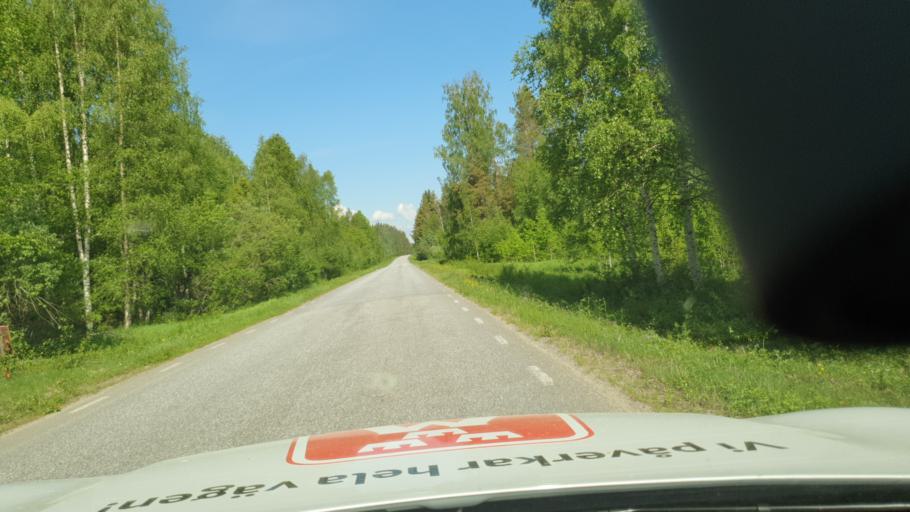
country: SE
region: Vaesterbotten
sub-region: Robertsfors Kommun
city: Robertsfors
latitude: 64.2437
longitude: 20.8490
